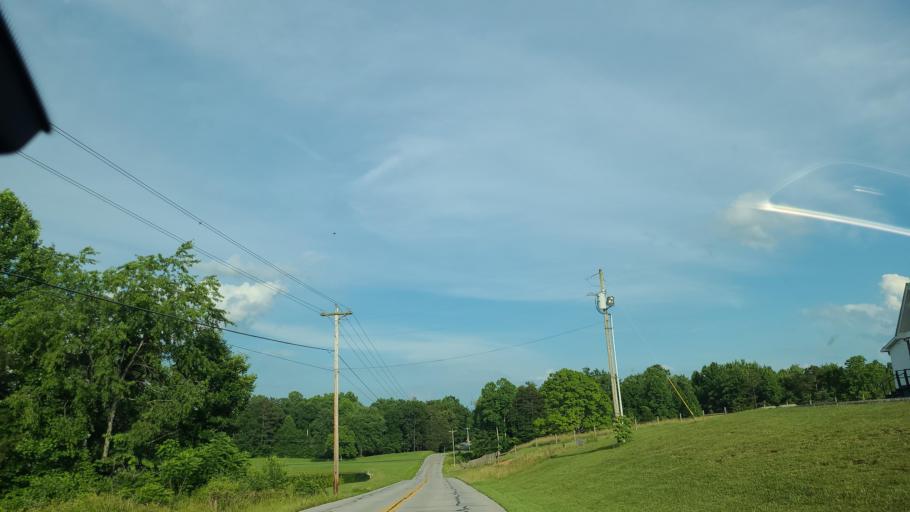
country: US
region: Kentucky
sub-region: Whitley County
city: Corbin
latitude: 36.8947
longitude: -84.2296
